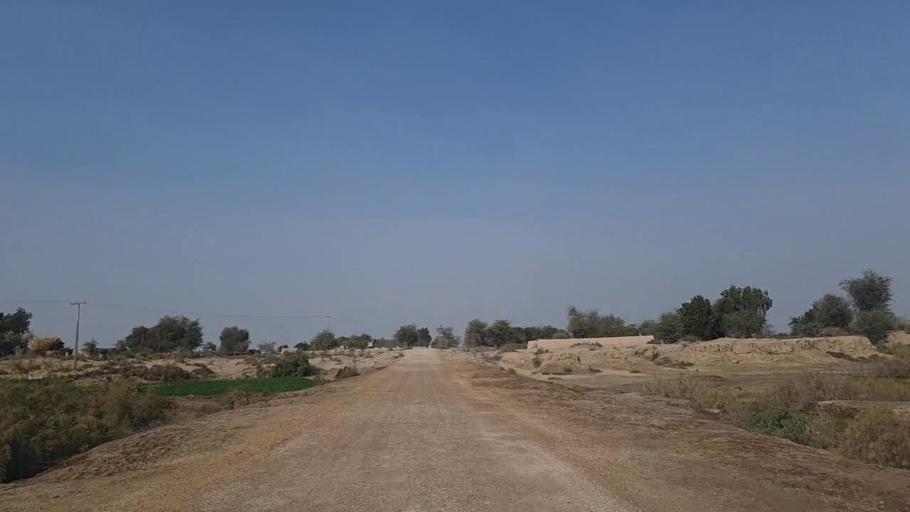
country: PK
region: Sindh
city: Daur
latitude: 26.5139
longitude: 68.4814
